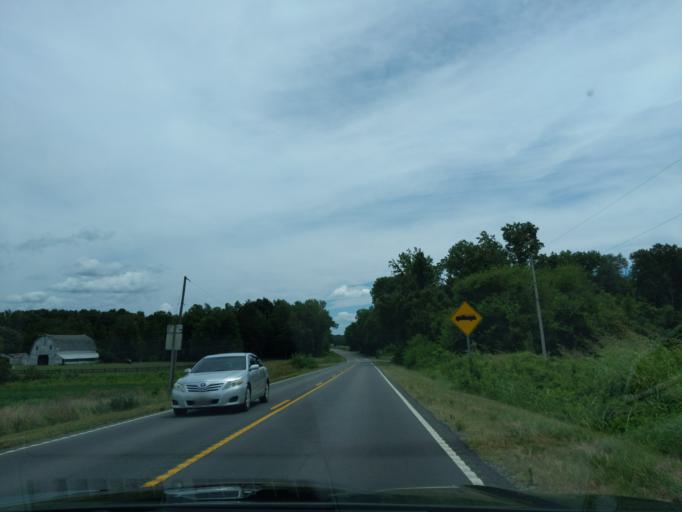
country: US
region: North Carolina
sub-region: Cabarrus County
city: Mount Pleasant
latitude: 35.4390
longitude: -80.3711
